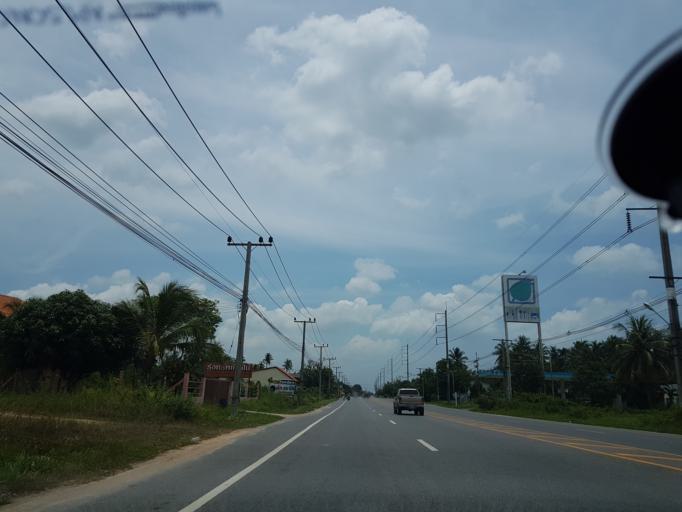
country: TH
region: Songkhla
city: Songkhla
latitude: 7.0987
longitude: 100.6338
